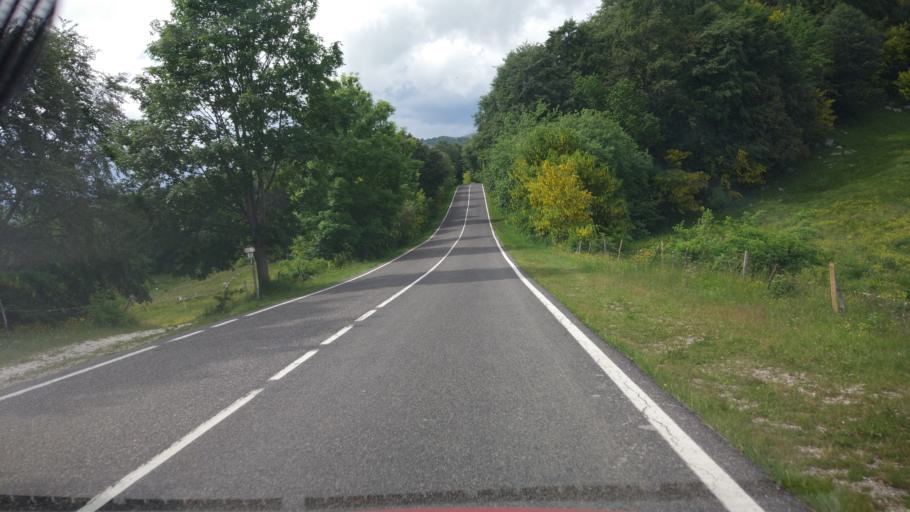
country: IT
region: Veneto
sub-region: Provincia di Verona
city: Velo Veronese
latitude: 45.6586
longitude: 11.0872
